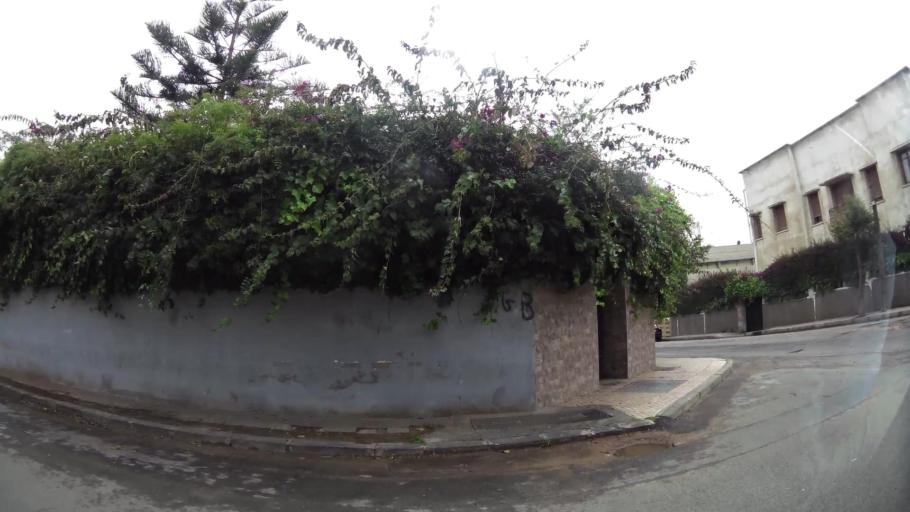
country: MA
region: Grand Casablanca
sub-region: Casablanca
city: Casablanca
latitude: 33.5779
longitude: -7.6108
